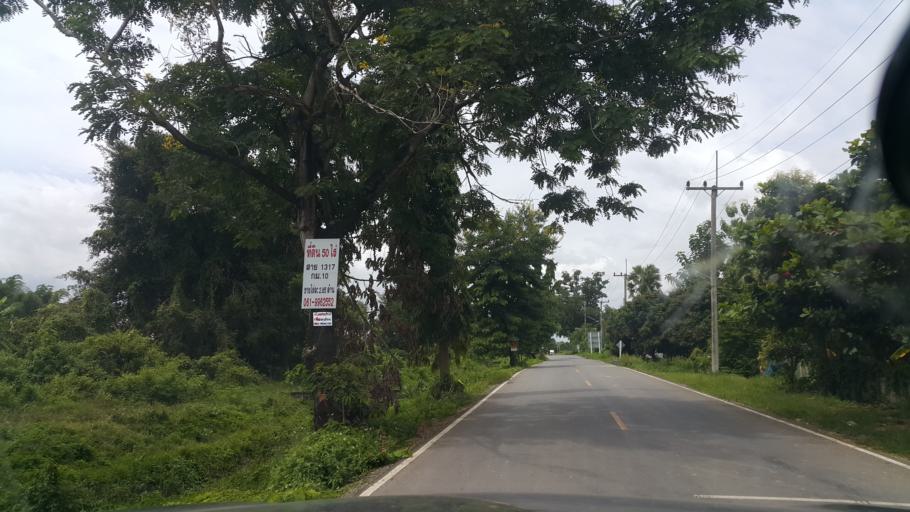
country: TH
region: Chiang Mai
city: San Kamphaeng
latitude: 18.7507
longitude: 99.1662
